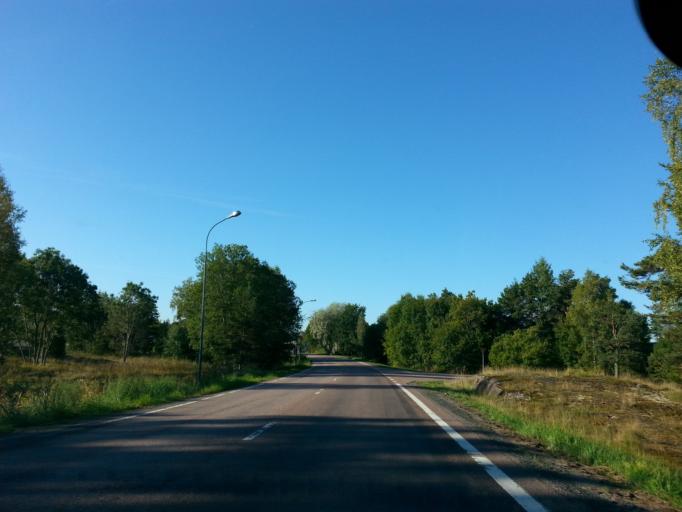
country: SE
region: Uppsala
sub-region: Osthammars Kommun
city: Oregrund
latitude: 60.3310
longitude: 18.4284
